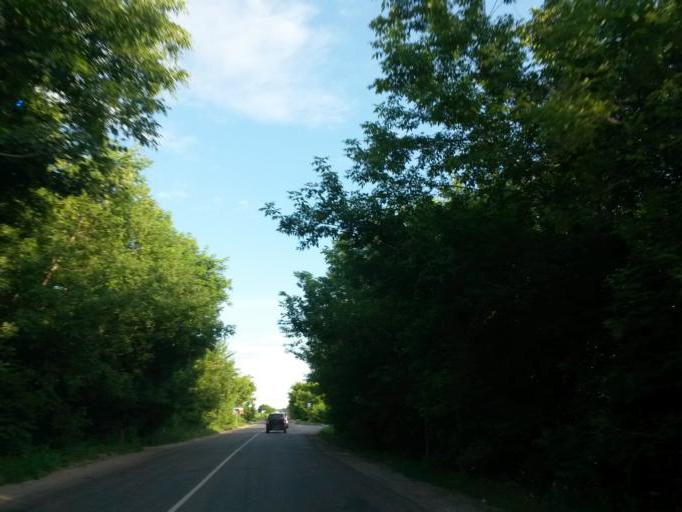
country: RU
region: Moskovskaya
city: Domodedovo
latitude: 55.4435
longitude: 37.6752
